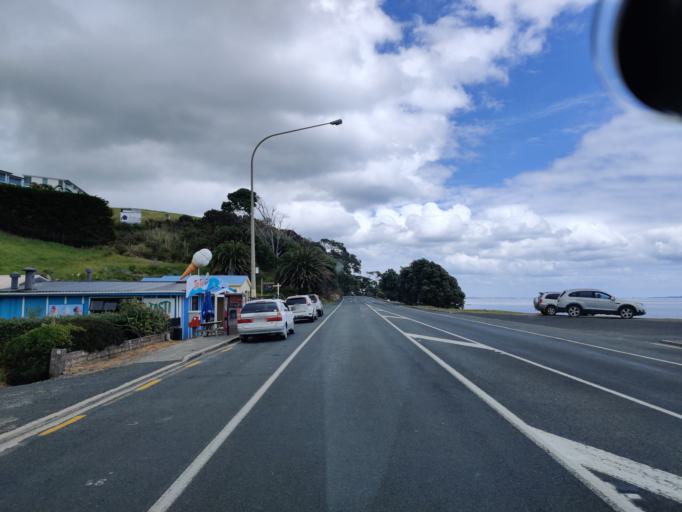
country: NZ
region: Northland
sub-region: Far North District
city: Taipa
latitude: -34.9909
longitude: 173.4839
